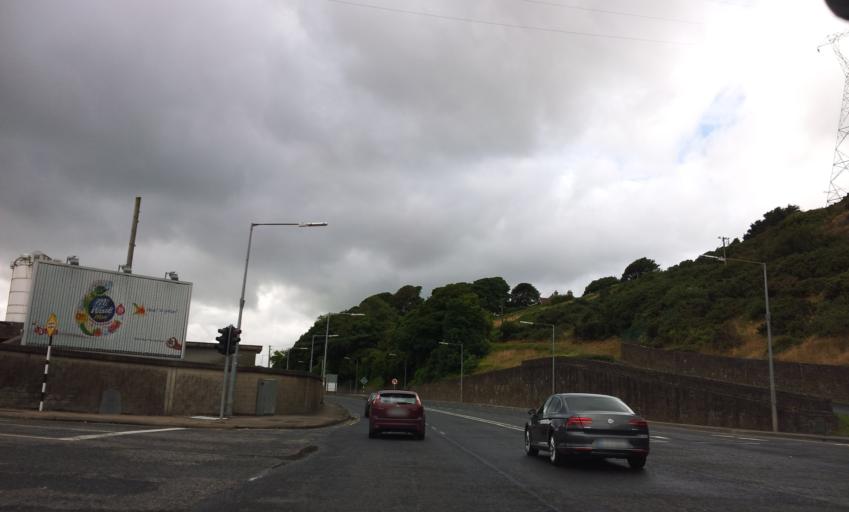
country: IE
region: Munster
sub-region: Waterford
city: Waterford
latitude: 52.2679
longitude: -7.1235
